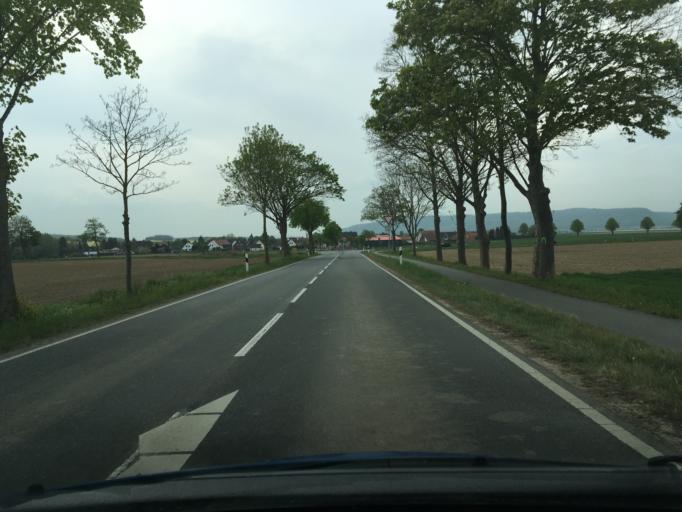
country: DE
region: Lower Saxony
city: Elze
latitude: 52.1702
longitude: 9.7107
